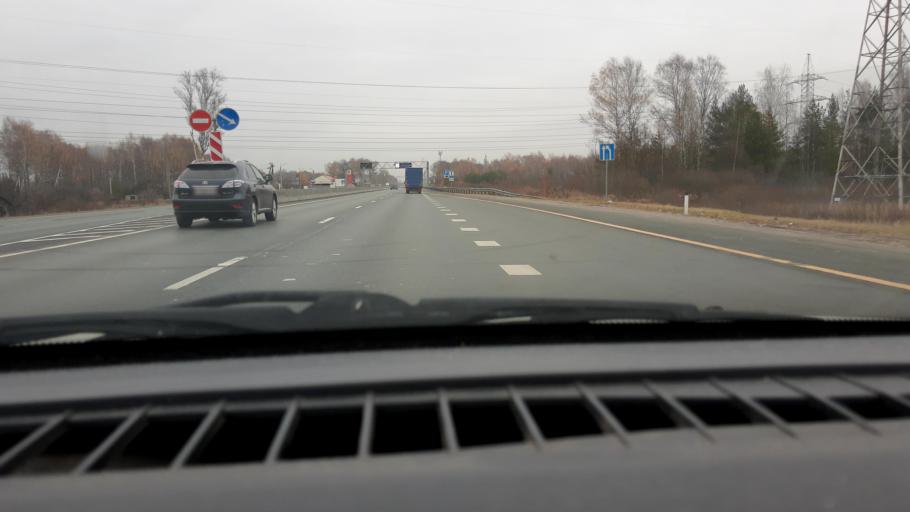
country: RU
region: Nizjnij Novgorod
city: Babino
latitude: 56.3058
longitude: 43.6624
